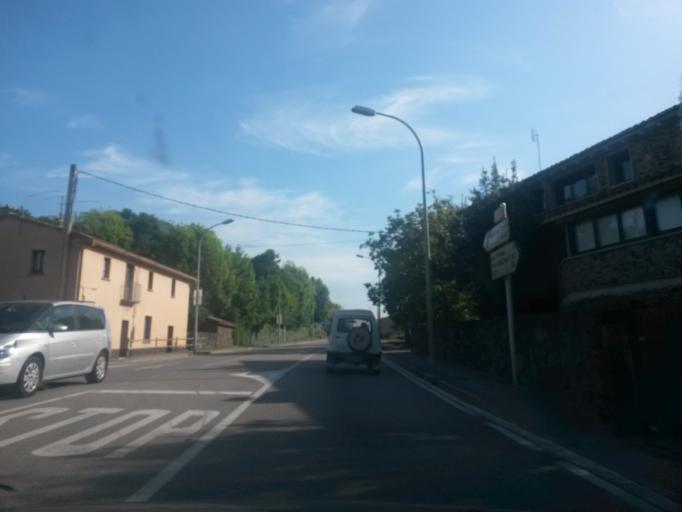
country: ES
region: Catalonia
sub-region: Provincia de Girona
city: Olot
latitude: 42.1572
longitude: 2.4659
